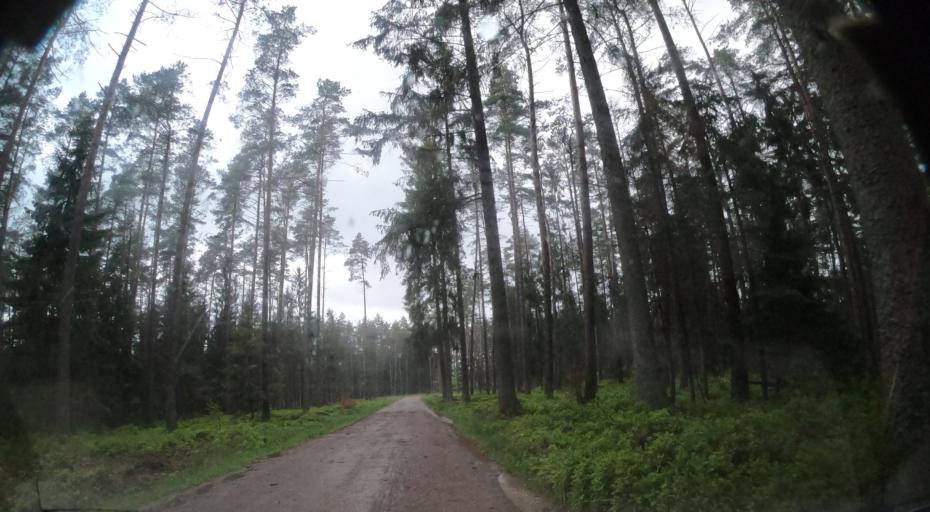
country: PL
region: West Pomeranian Voivodeship
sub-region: Powiat koszalinski
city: Polanow
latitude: 54.1372
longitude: 16.4844
